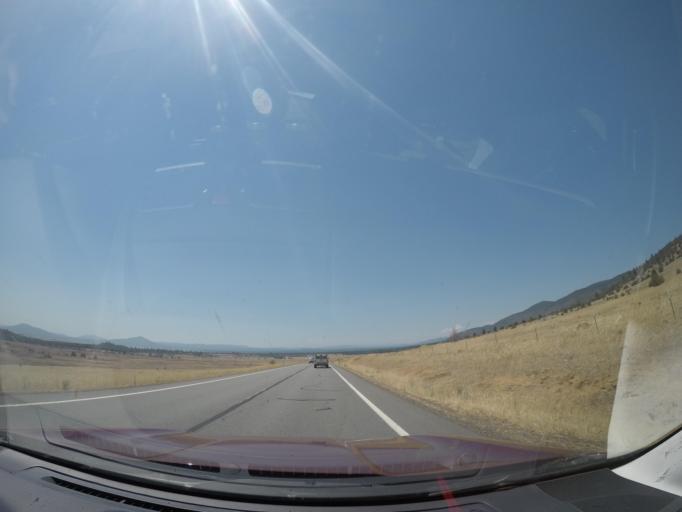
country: US
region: California
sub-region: Shasta County
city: Burney
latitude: 41.0962
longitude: -121.2826
